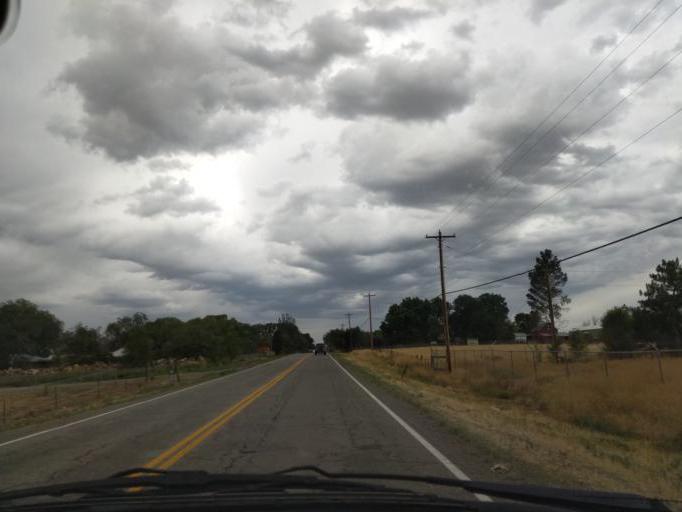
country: US
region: Colorado
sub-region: Delta County
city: Paonia
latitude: 38.7999
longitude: -107.7575
